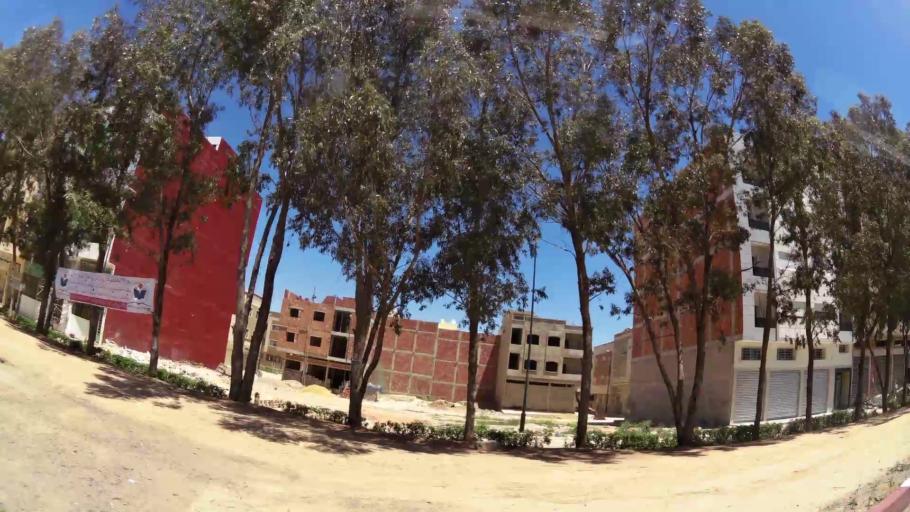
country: MA
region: Meknes-Tafilalet
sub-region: Meknes
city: Meknes
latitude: 33.8523
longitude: -5.5651
